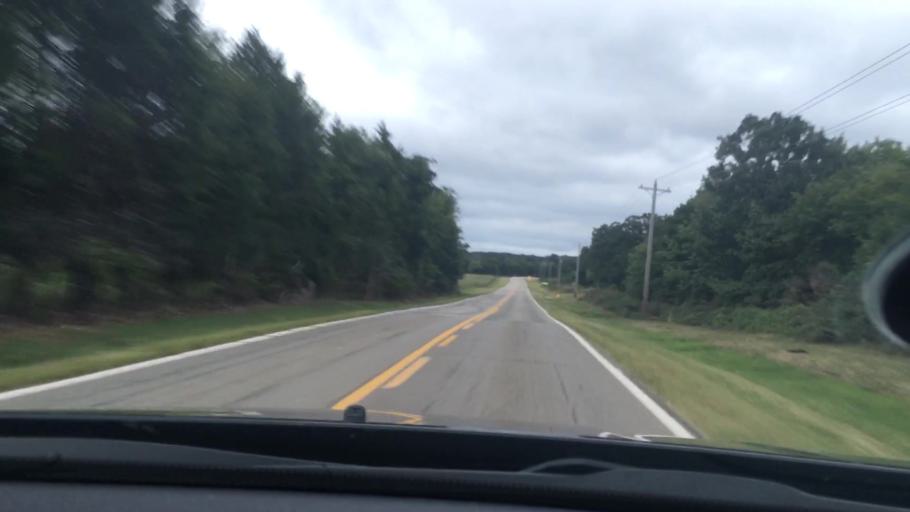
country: US
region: Oklahoma
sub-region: Sequoyah County
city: Vian
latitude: 35.6049
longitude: -95.0019
